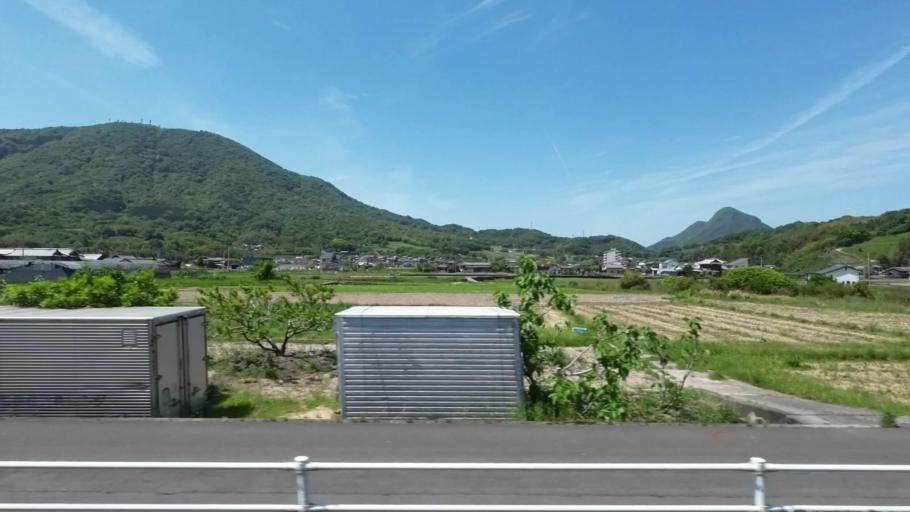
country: JP
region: Kagawa
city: Marugame
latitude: 34.2178
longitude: 133.7978
